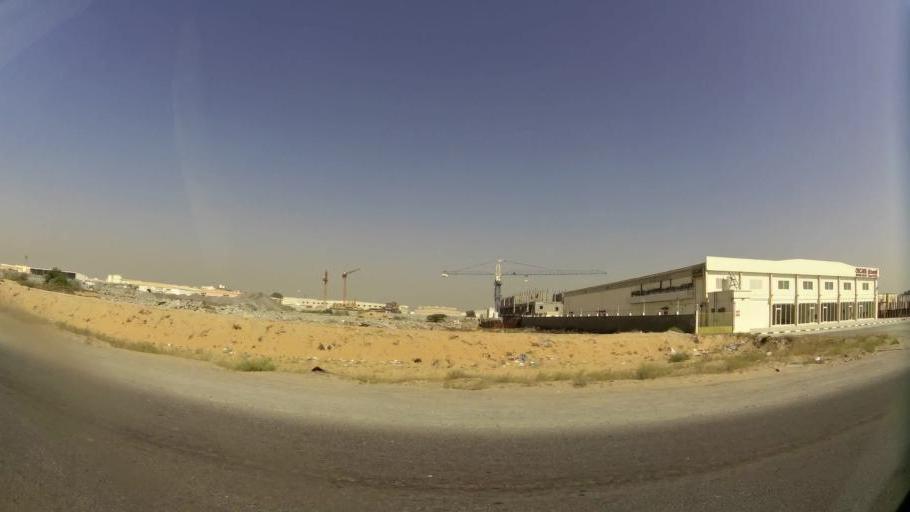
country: AE
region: Ajman
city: Ajman
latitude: 25.4301
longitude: 55.5349
